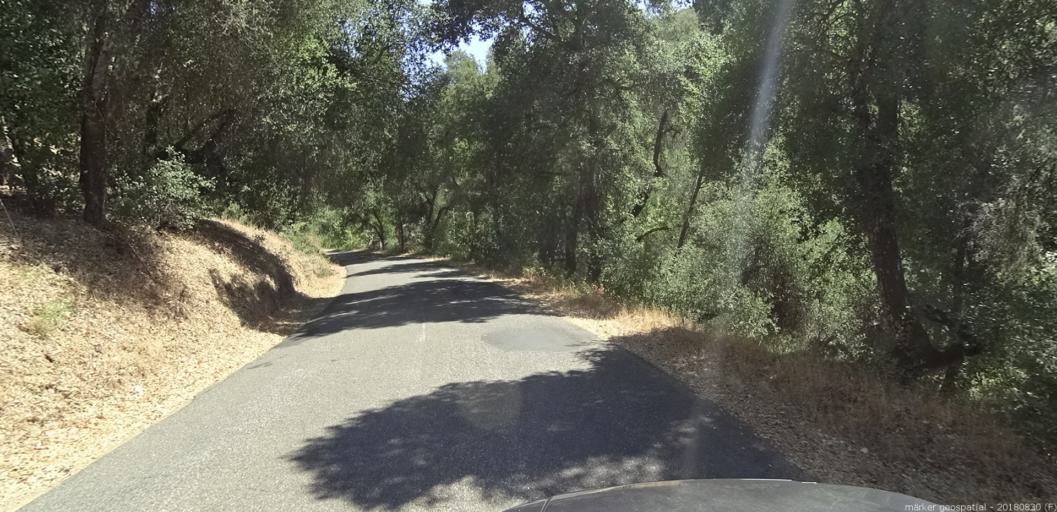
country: US
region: California
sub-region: Monterey County
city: King City
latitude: 36.0092
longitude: -121.4051
